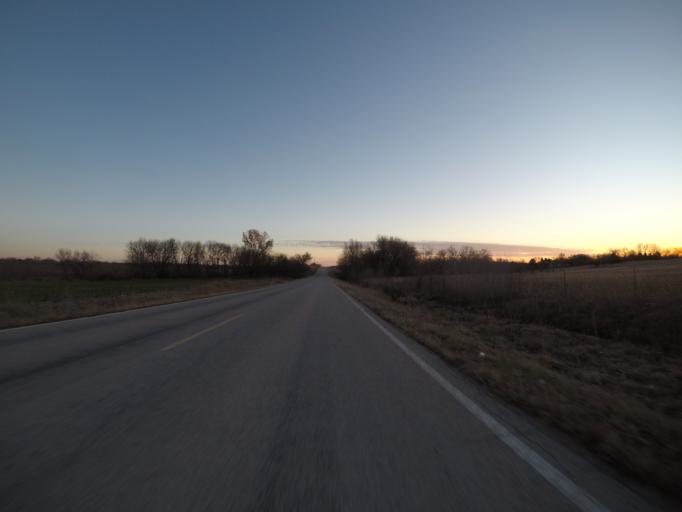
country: US
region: Kansas
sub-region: Riley County
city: Manhattan
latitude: 39.2294
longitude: -96.4825
